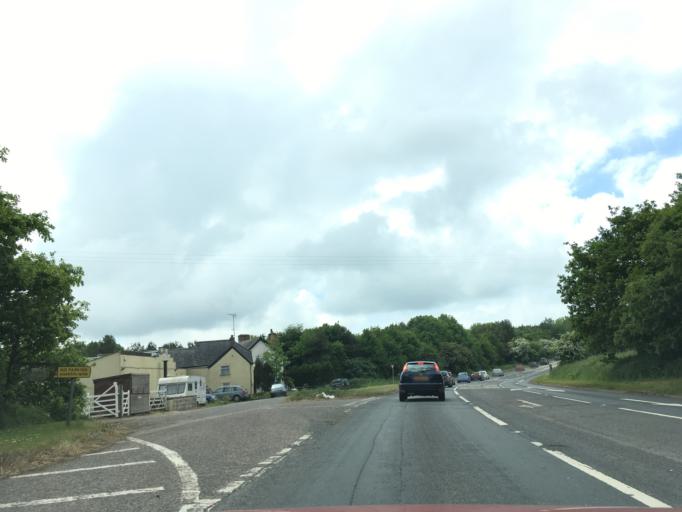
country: GB
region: England
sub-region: Devon
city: Uffculme
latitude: 50.9233
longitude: -3.3255
